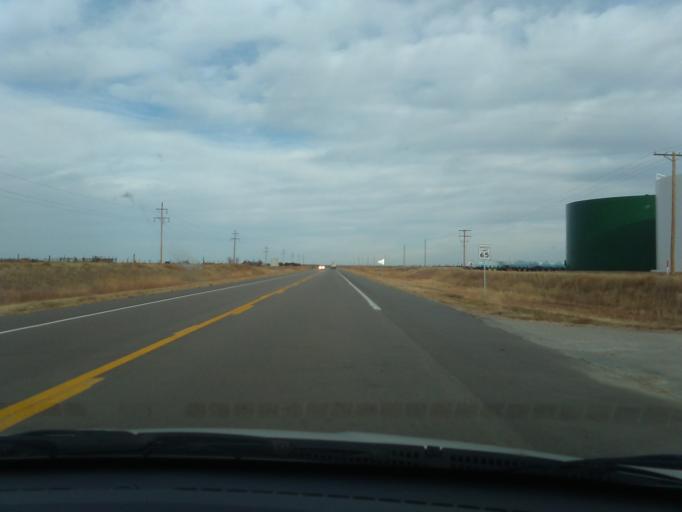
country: US
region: Nebraska
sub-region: Dundy County
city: Benkelman
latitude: 40.0635
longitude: -101.5287
